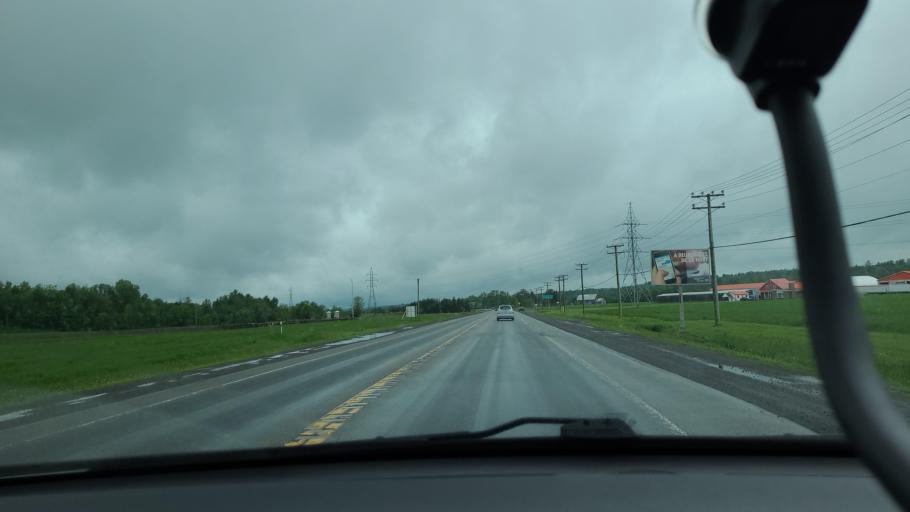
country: CA
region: Quebec
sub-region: Laurentides
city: Saint-Jerome
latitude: 45.7463
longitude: -74.0145
